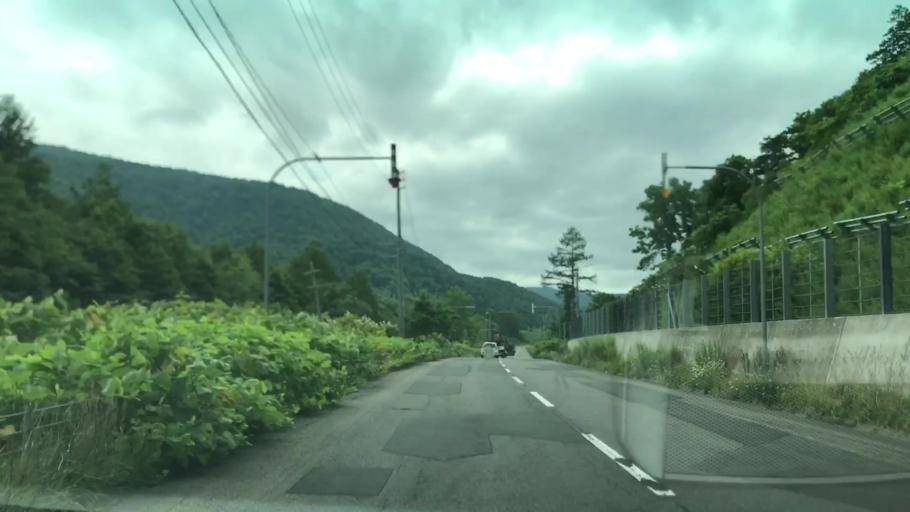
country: JP
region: Hokkaido
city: Yoichi
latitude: 43.0354
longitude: 140.8635
